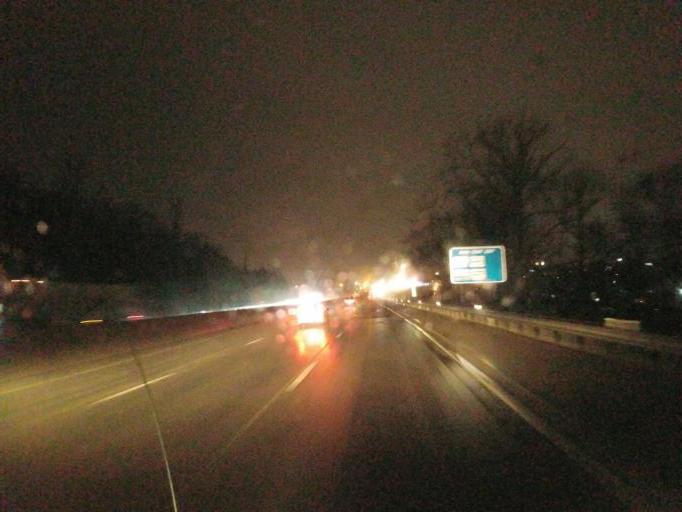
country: US
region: Missouri
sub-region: Franklin County
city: Pacific
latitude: 38.4879
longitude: -90.7486
